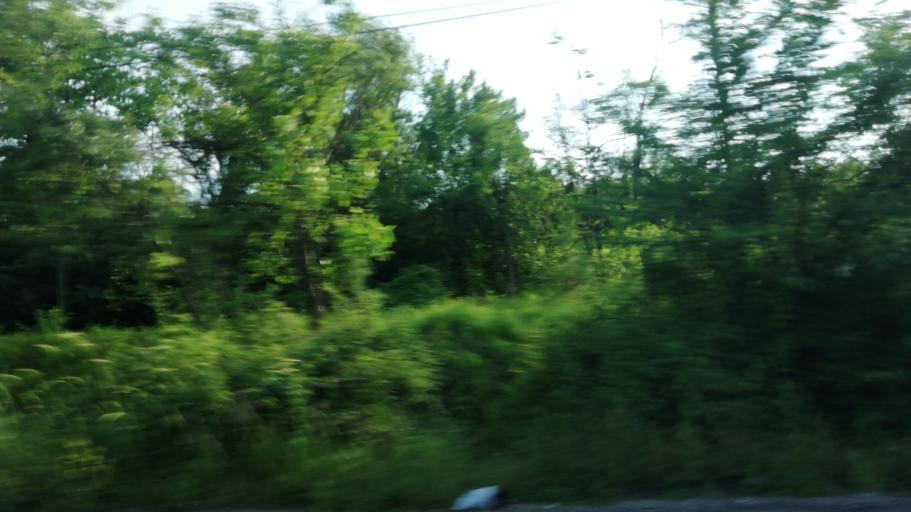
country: TR
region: Karabuk
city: Karabuk
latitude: 41.1404
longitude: 32.6306
